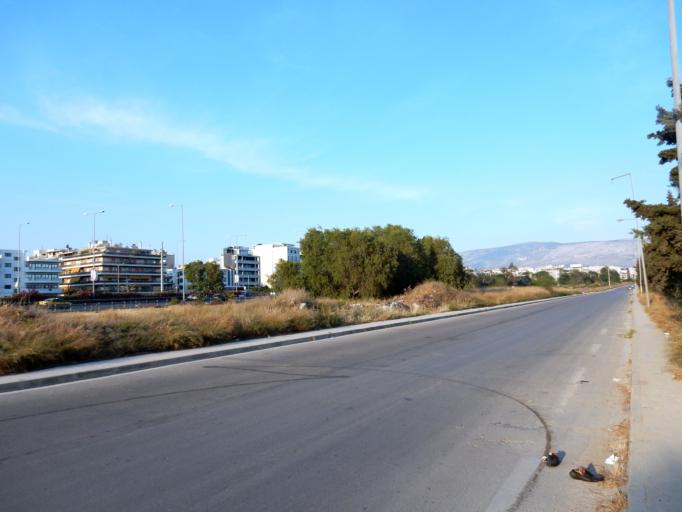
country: GR
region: Attica
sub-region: Nomarchia Athinas
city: Moskhaton
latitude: 37.9435
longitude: 23.6755
